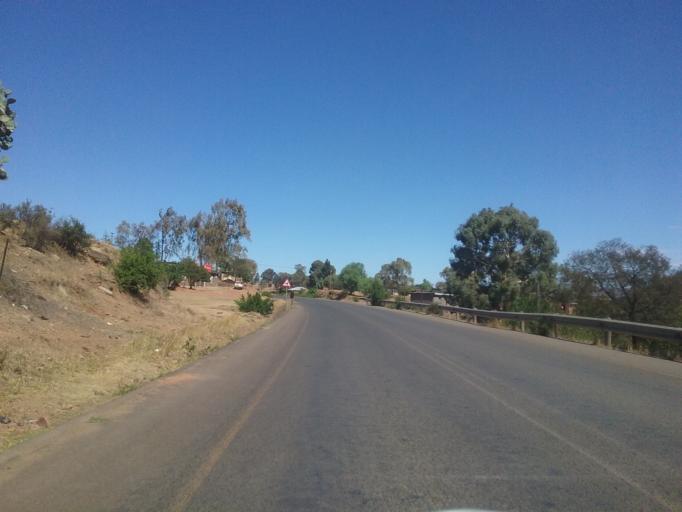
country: LS
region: Quthing
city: Quthing
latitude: -30.3996
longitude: 27.6719
